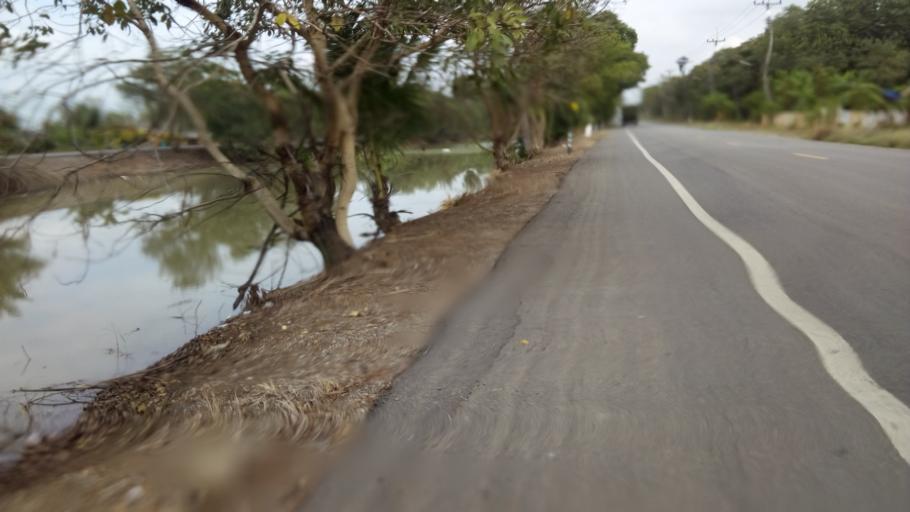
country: TH
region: Pathum Thani
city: Nong Suea
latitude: 14.2241
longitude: 100.8233
